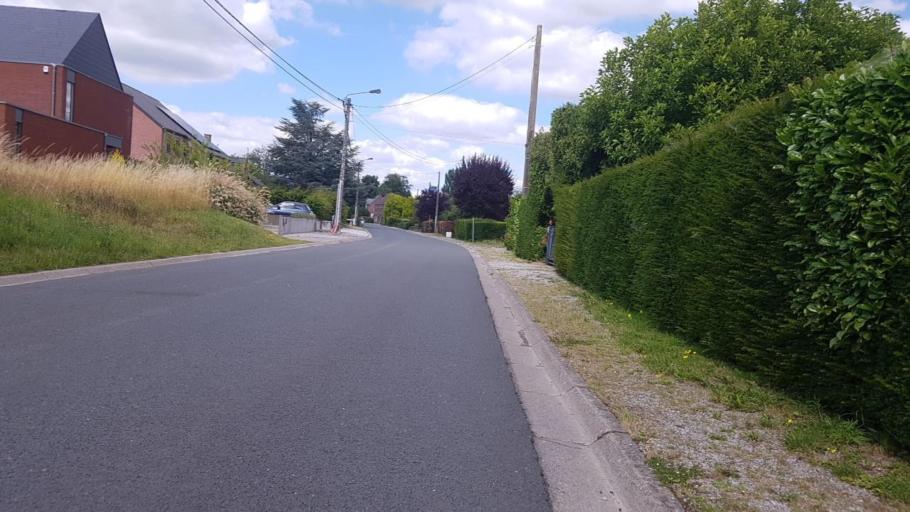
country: BE
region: Wallonia
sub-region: Province du Hainaut
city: Charleroi
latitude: 50.3351
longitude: 4.3902
